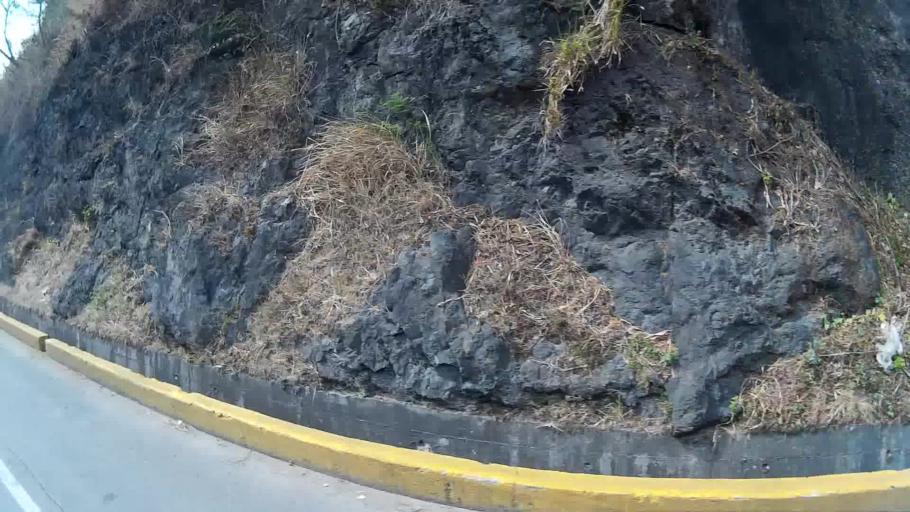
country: CO
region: Risaralda
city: Pereira
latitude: 4.8127
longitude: -75.7490
